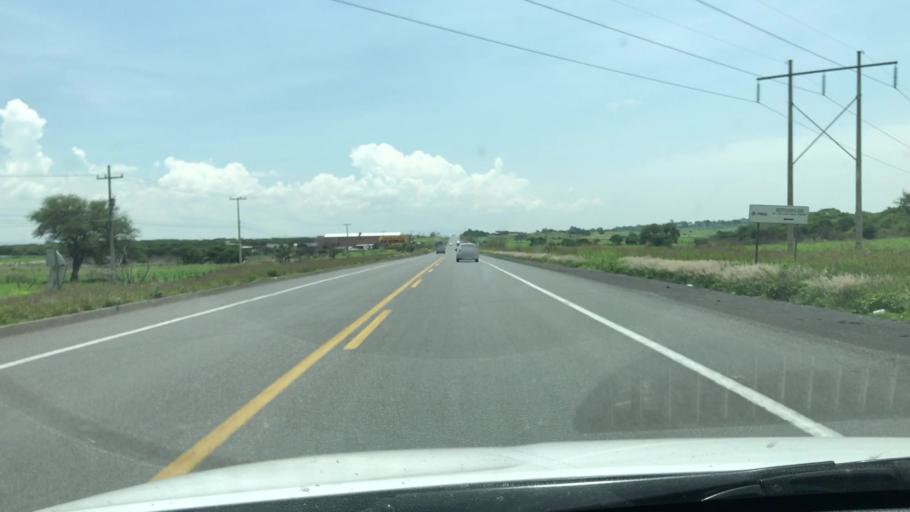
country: MX
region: Jalisco
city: Degollado
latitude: 20.3620
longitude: -102.1454
